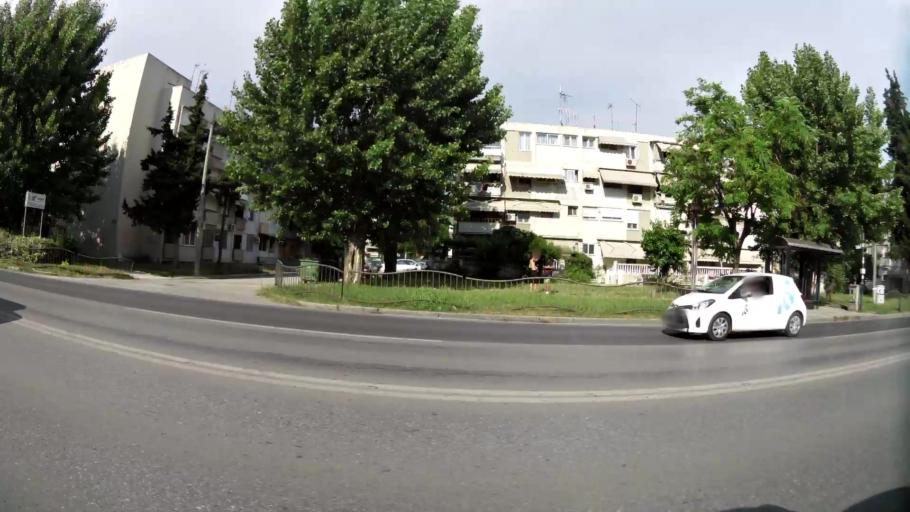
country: GR
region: Central Macedonia
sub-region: Nomos Thessalonikis
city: Kalamaria
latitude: 40.5701
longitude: 22.9732
